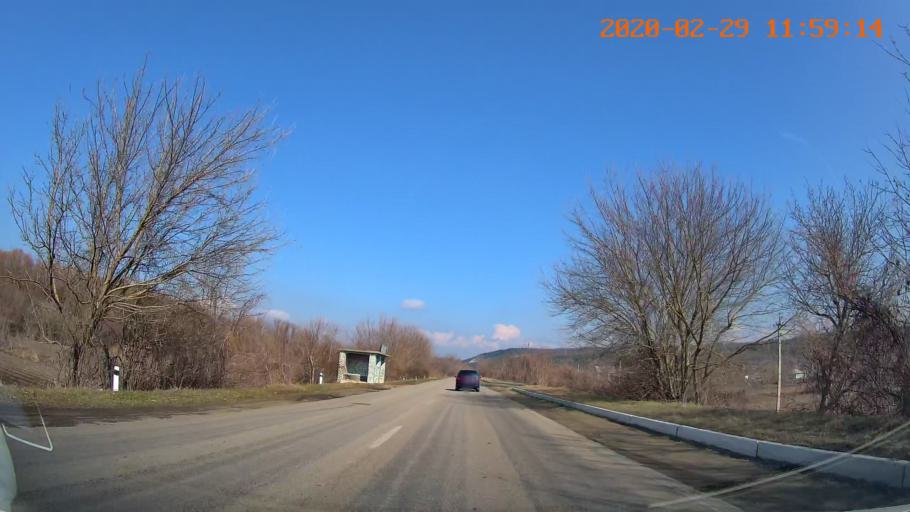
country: MD
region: Telenesti
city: Ribnita
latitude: 47.8227
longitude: 29.0158
